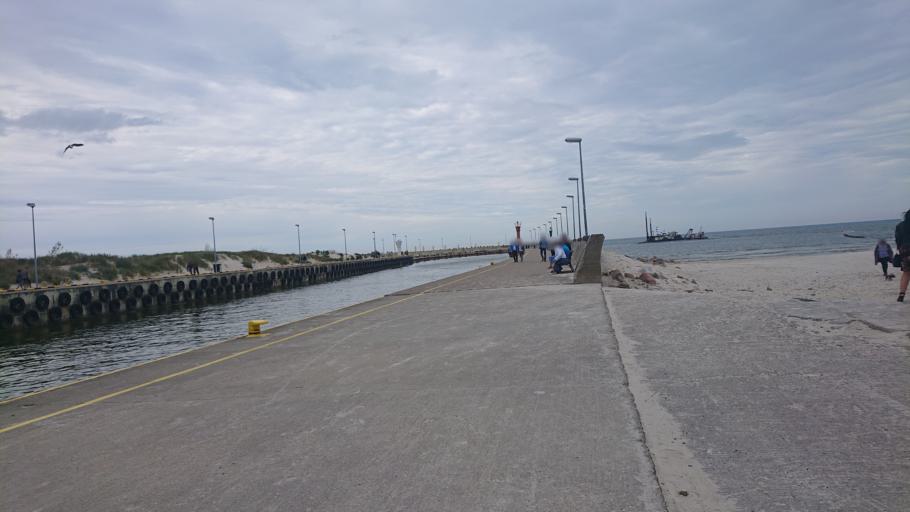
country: PL
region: Pomeranian Voivodeship
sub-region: Powiat leborski
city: Leba
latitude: 54.7673
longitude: 17.5515
